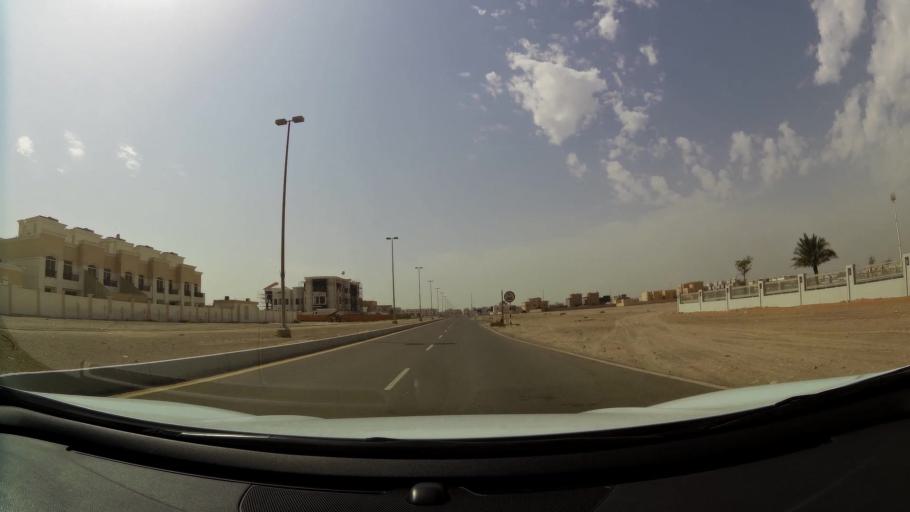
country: AE
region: Abu Dhabi
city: Abu Dhabi
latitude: 24.3323
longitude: 54.5570
